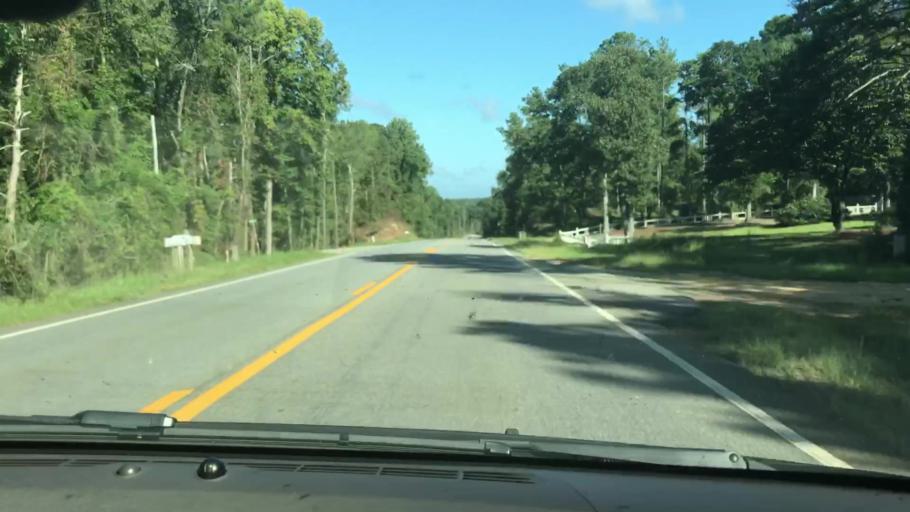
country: US
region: Georgia
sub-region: Quitman County
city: Georgetown
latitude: 31.8664
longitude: -85.0741
